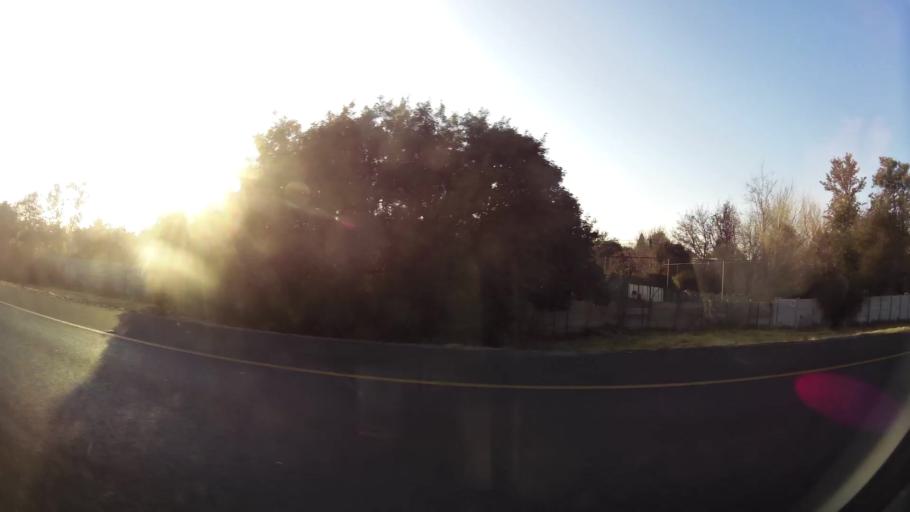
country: ZA
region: Orange Free State
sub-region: Mangaung Metropolitan Municipality
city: Bloemfontein
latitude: -29.1076
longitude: 26.1642
